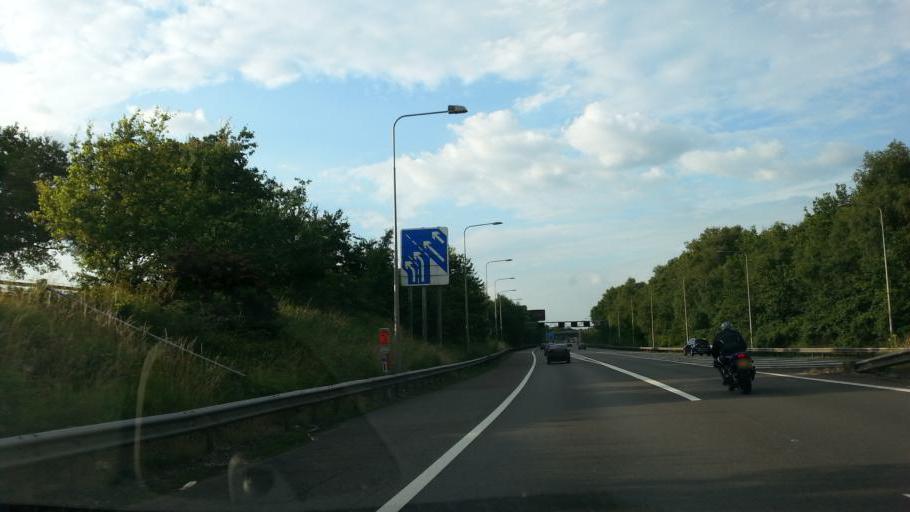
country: GB
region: England
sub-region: Solihull
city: Cheswick Green
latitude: 52.3510
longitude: -1.8100
